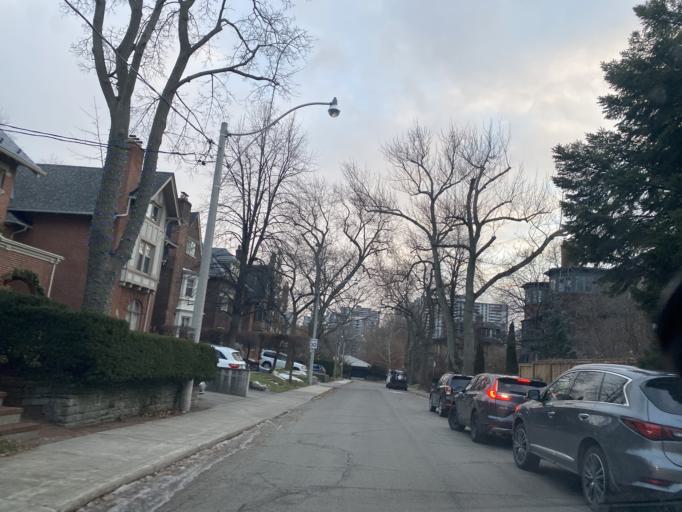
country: CA
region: Ontario
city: Toronto
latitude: 43.6751
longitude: -79.3736
